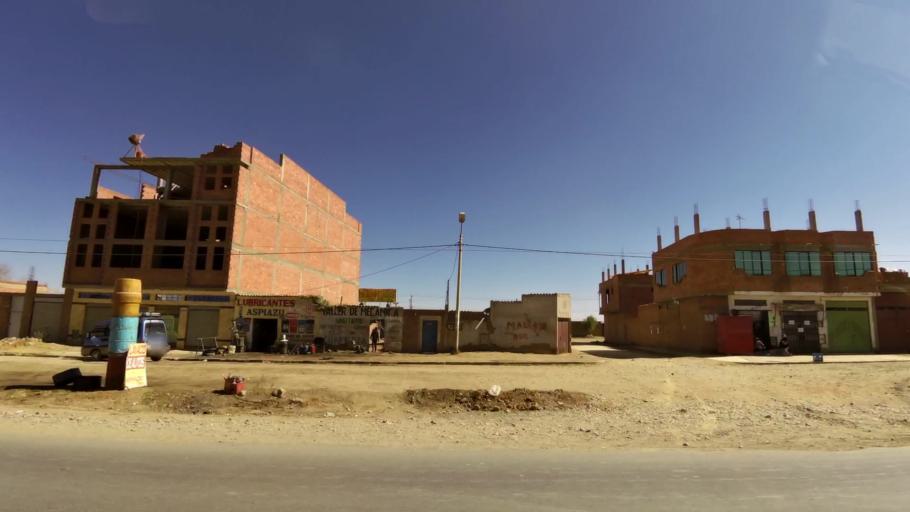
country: BO
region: La Paz
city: La Paz
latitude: -16.5593
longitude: -68.2136
